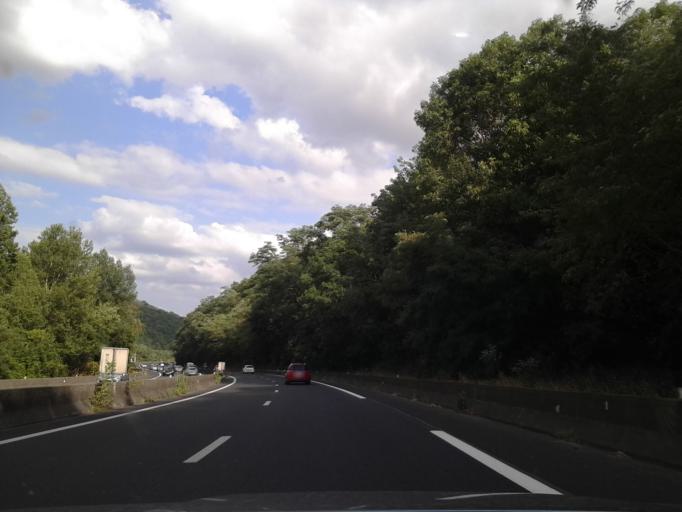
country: FR
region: Auvergne
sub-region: Departement du Puy-de-Dome
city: Issoire
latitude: 45.5744
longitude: 3.2415
